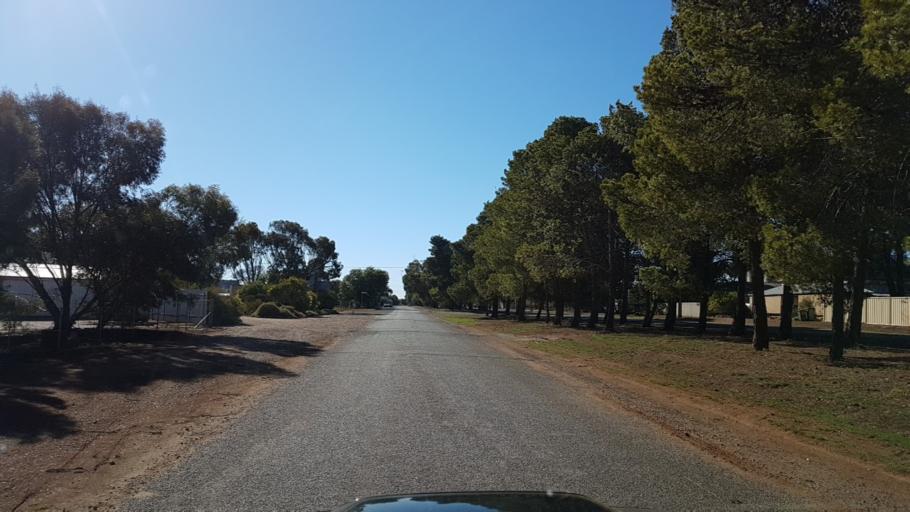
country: AU
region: South Australia
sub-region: Peterborough
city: Peterborough
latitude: -33.0317
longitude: 138.7497
